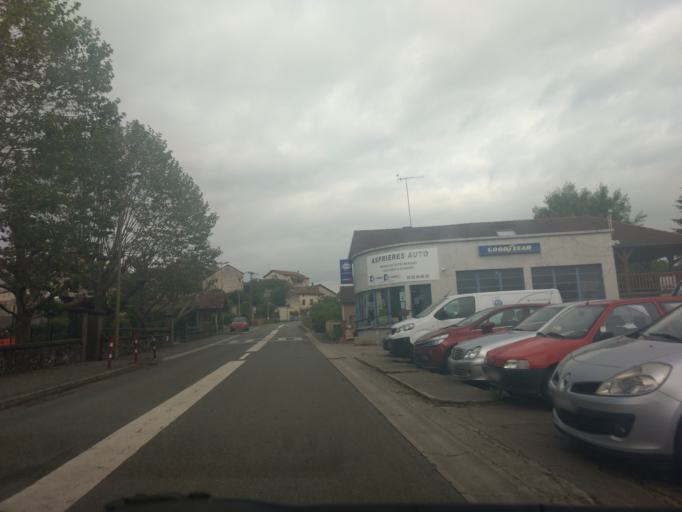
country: FR
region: Midi-Pyrenees
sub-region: Departement de l'Aveyron
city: Capdenac-Gare
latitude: 44.5448
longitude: 2.1421
